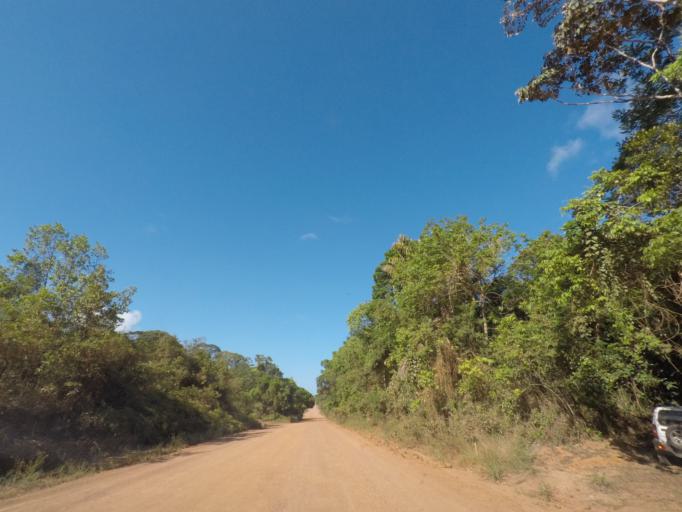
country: BR
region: Bahia
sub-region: Marau
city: Marau
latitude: -14.1200
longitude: -38.9887
